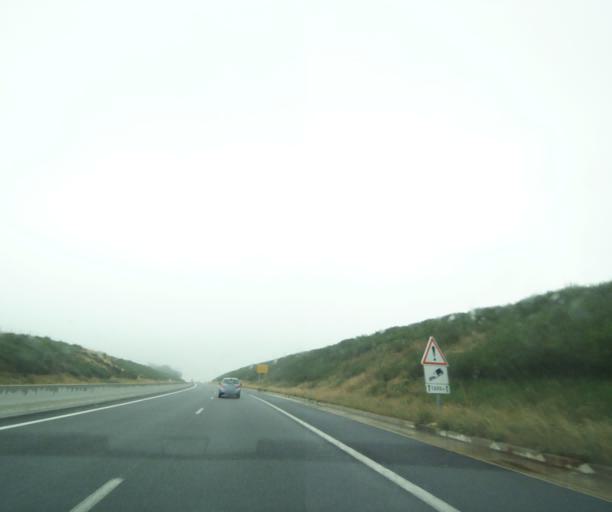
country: FR
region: Midi-Pyrenees
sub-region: Departement de l'Aveyron
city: Baraqueville
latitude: 44.2169
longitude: 2.4071
